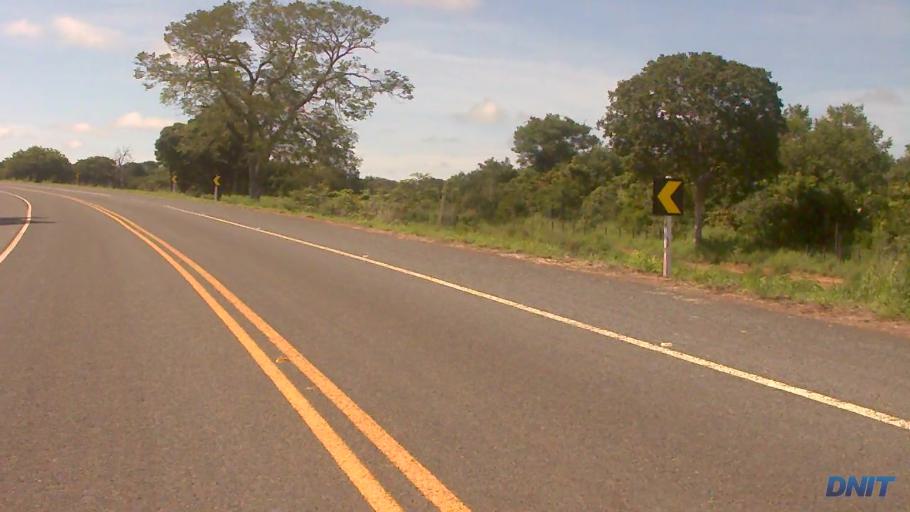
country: BR
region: Goias
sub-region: Sao Miguel Do Araguaia
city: Sao Miguel do Araguaia
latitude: -13.3129
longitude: -50.1707
